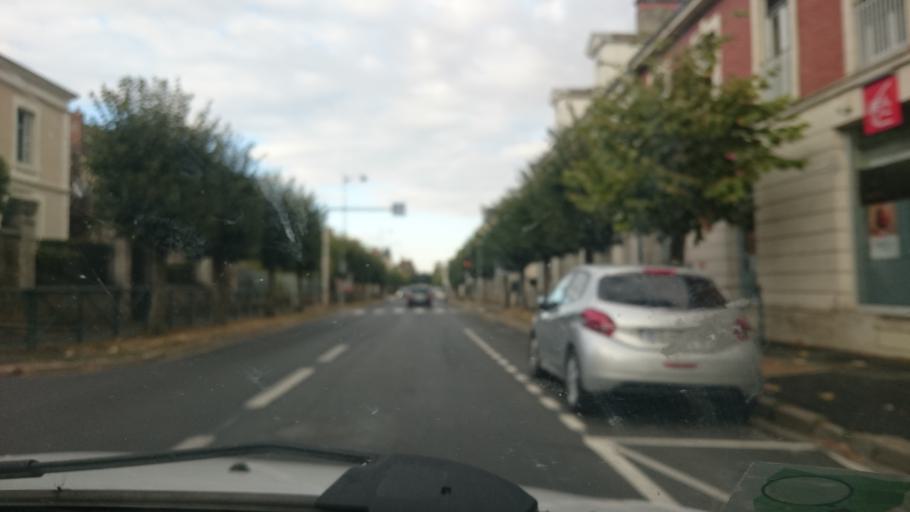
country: FR
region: Centre
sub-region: Departement de l'Indre
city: La Chatre
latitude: 46.5827
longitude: 1.9847
